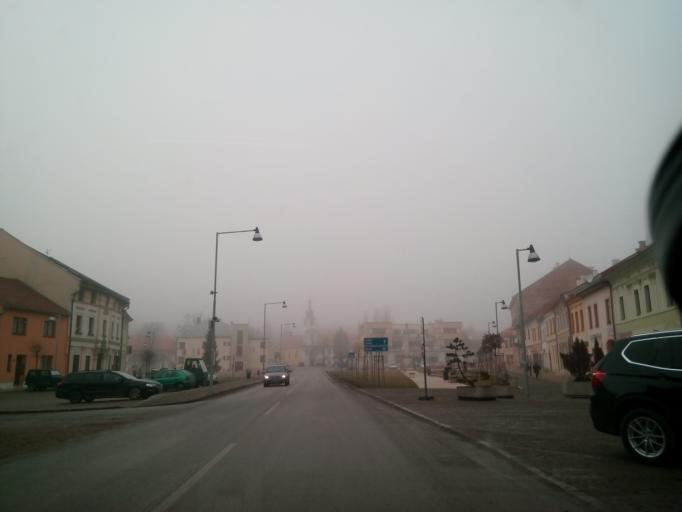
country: SK
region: Presovsky
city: Spisske Podhradie
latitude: 48.9998
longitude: 20.7538
